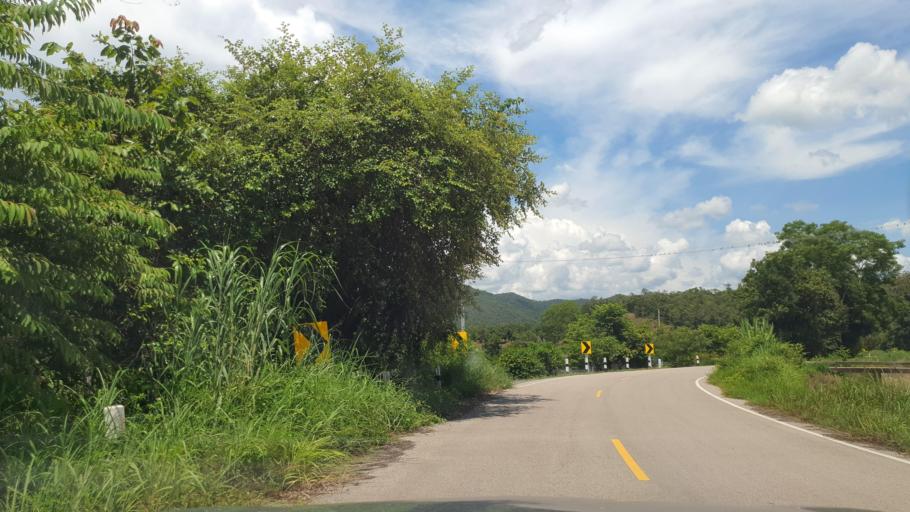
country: TH
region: Chiang Mai
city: Mae On
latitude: 18.7816
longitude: 99.1946
